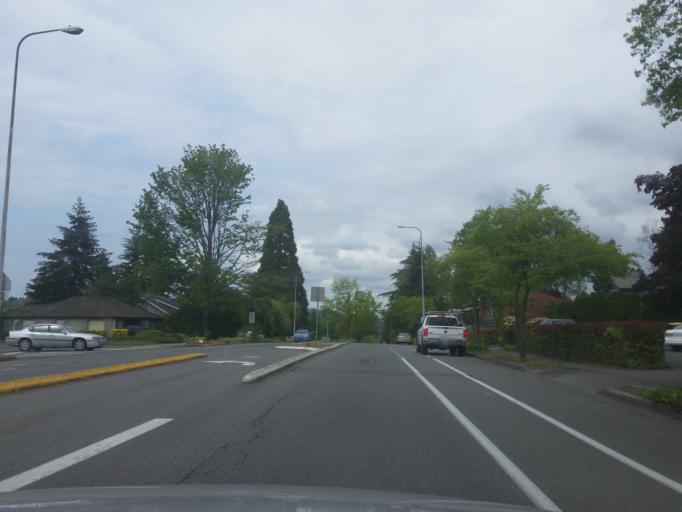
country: US
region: Washington
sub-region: King County
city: Kirkland
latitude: 47.6876
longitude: -122.2098
